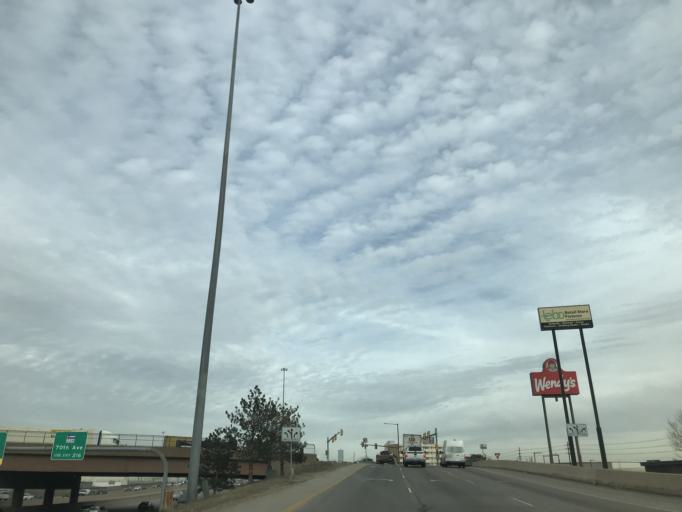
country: US
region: Colorado
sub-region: Adams County
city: Twin Lakes
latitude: 39.8008
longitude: -104.9845
